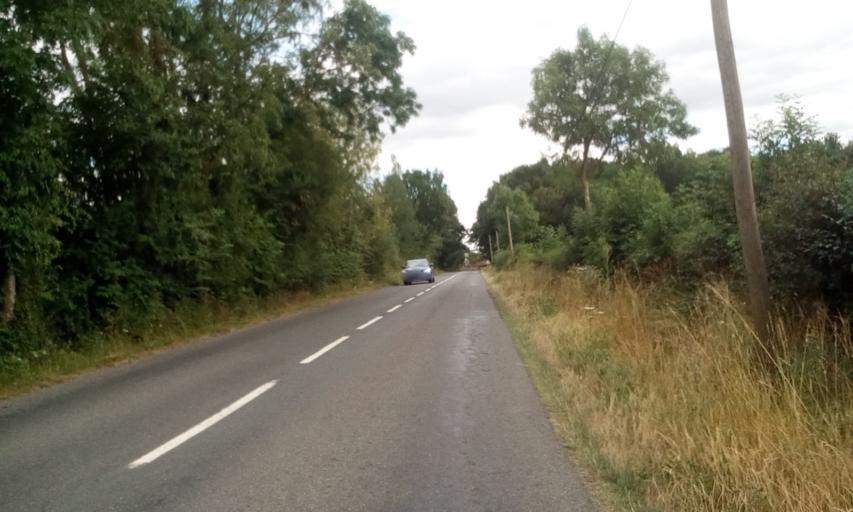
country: FR
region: Lower Normandy
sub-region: Departement du Calvados
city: Troarn
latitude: 49.1622
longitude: -0.1771
